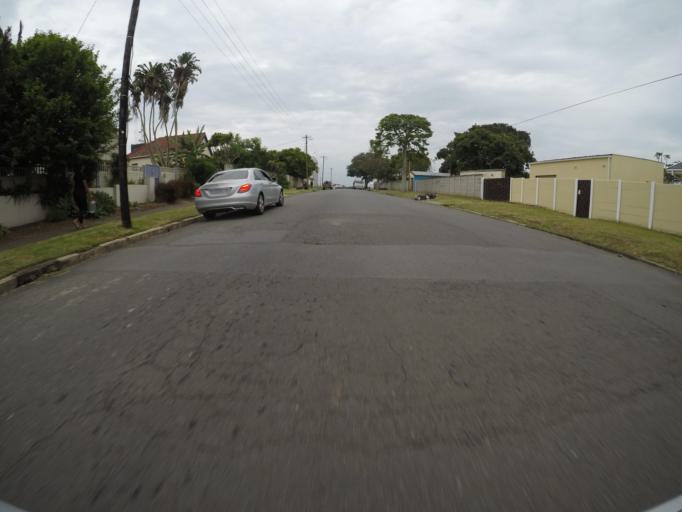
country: ZA
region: Eastern Cape
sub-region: Buffalo City Metropolitan Municipality
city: East London
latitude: -32.9756
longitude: 27.8941
